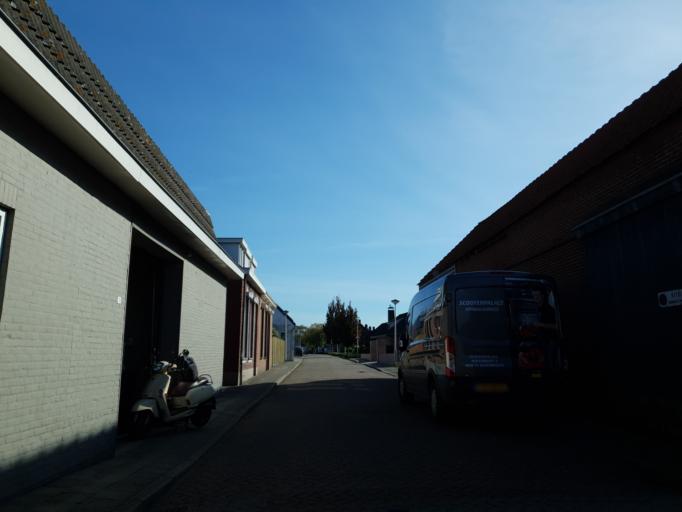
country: NL
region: North Brabant
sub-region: Gemeente Woensdrecht
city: Woensdrecht
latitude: 51.3952
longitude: 4.3299
